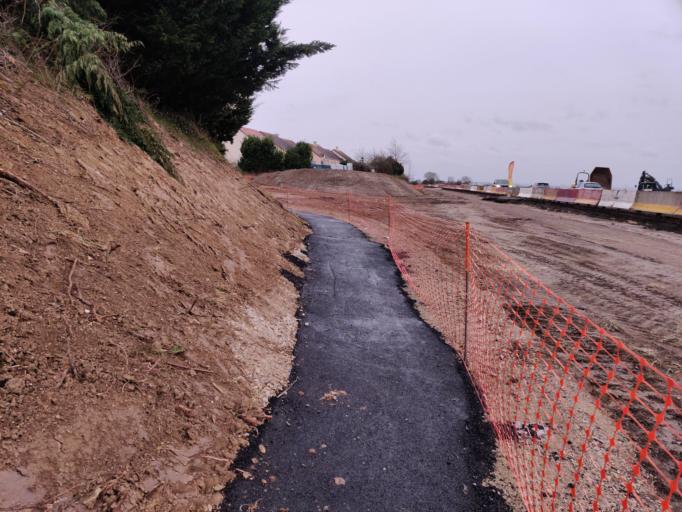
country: FR
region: Ile-de-France
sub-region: Departement du Val-d'Oise
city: Fontenay-en-Parisis
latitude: 49.0304
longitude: 2.4476
